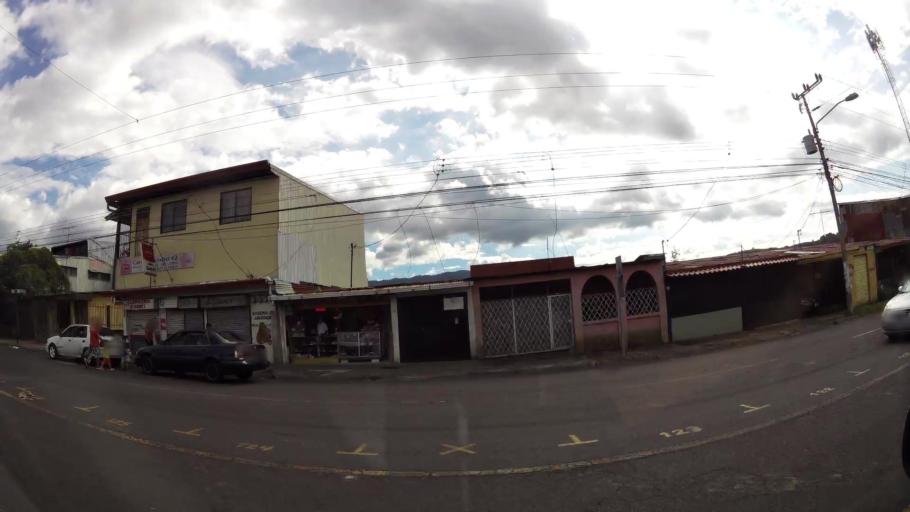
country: CR
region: Heredia
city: La Asuncion
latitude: 9.9591
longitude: -84.1619
